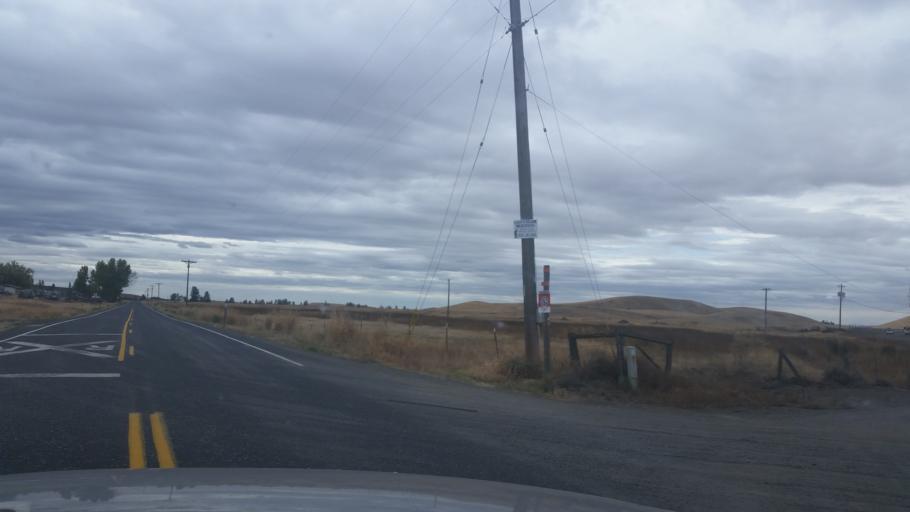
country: US
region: Washington
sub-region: Spokane County
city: Medical Lake
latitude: 47.5397
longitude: -117.8437
